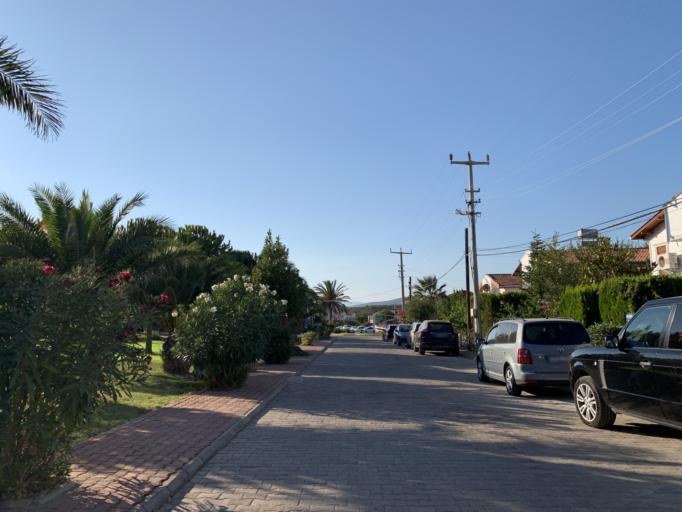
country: TR
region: Balikesir
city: Ayvalik
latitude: 39.3508
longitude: 26.6503
